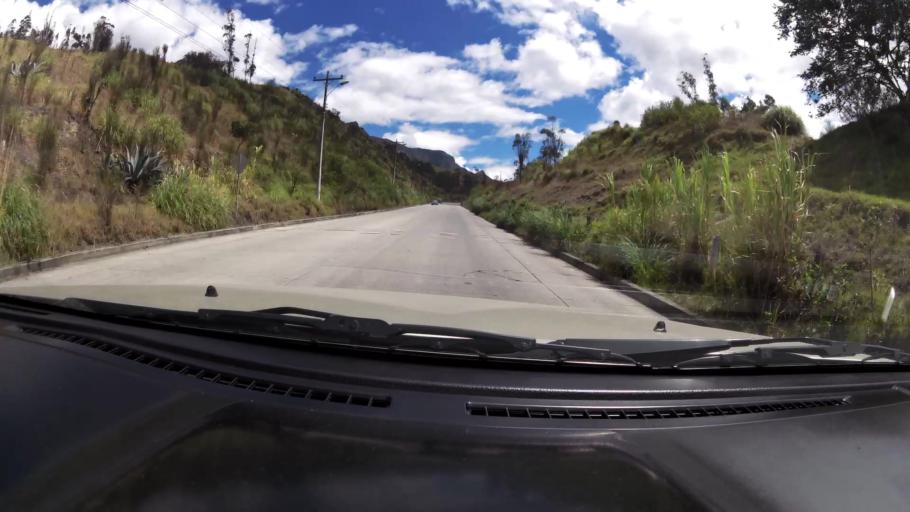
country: EC
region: Azuay
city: Cuenca
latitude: -3.1498
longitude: -79.1468
